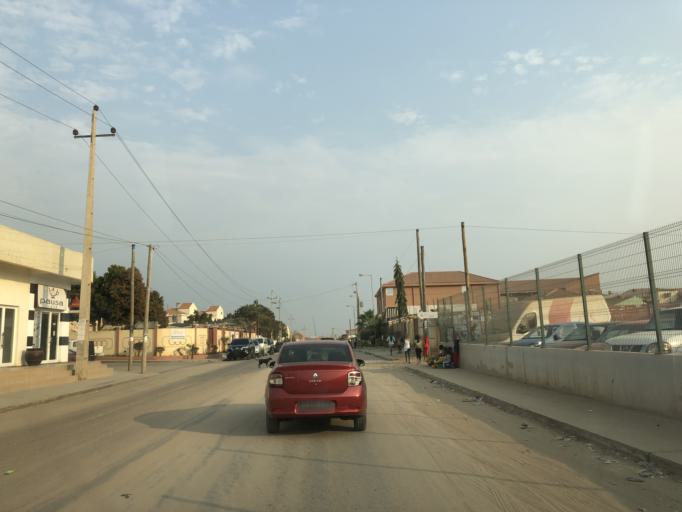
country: AO
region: Luanda
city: Luanda
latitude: -8.9094
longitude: 13.2080
